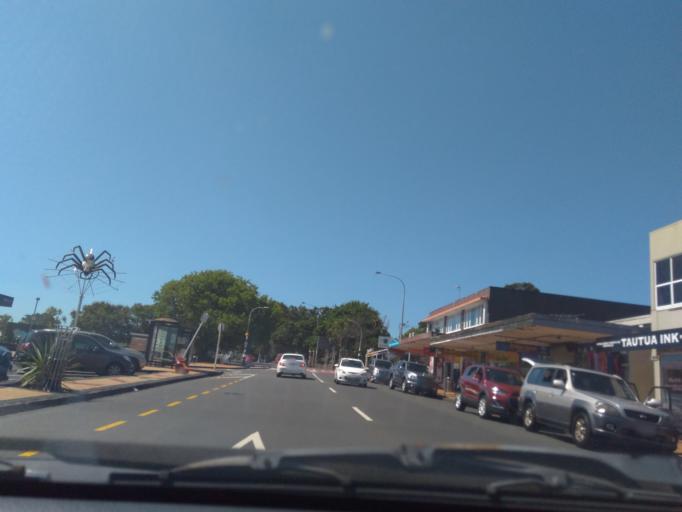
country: NZ
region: Auckland
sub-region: Auckland
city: Rosebank
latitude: -36.8972
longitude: 174.6971
